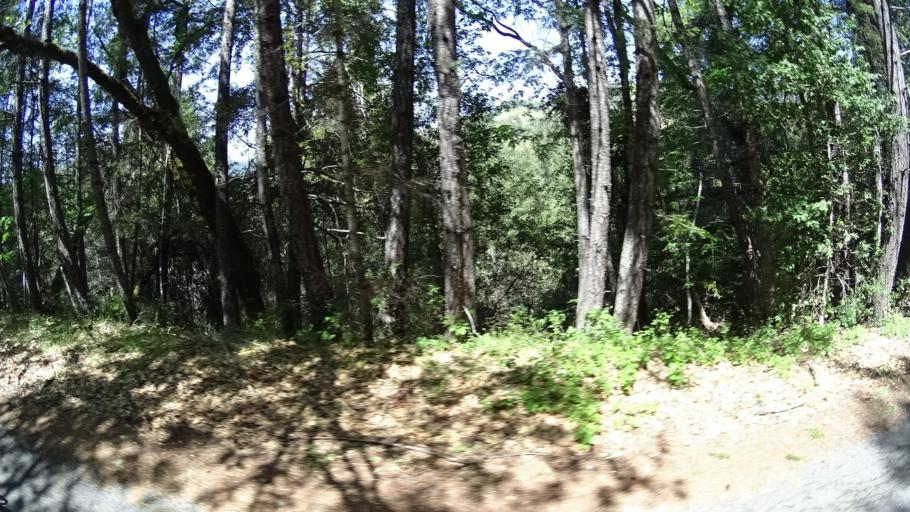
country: US
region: California
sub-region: Humboldt County
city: Redway
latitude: 40.1879
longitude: -123.5802
